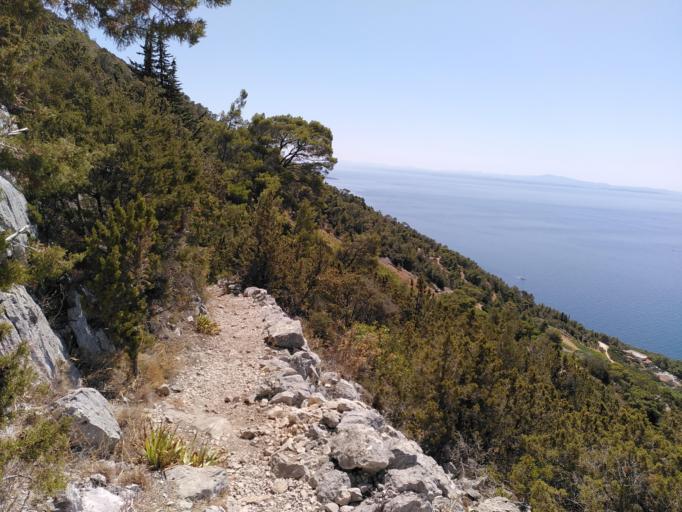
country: HR
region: Splitsko-Dalmatinska
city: Stari Grad
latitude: 43.1432
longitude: 16.5891
